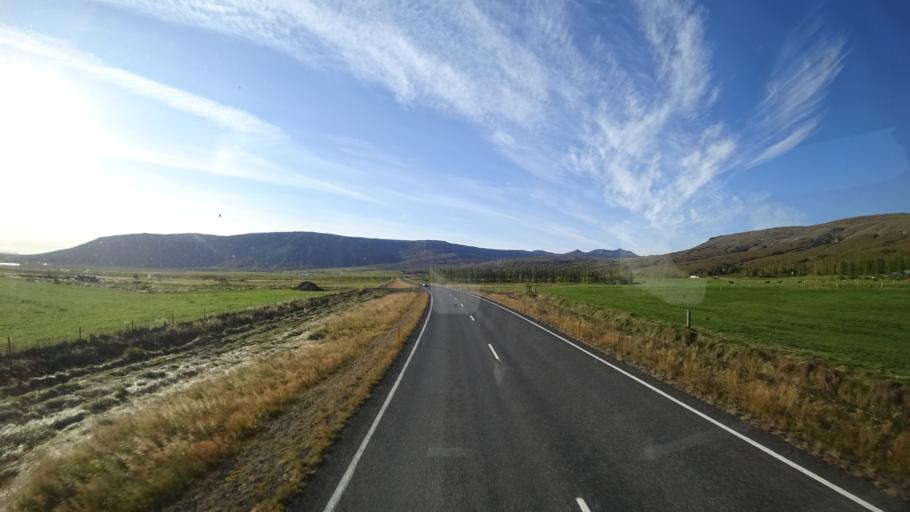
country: IS
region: South
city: Selfoss
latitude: 64.2357
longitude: -20.6414
